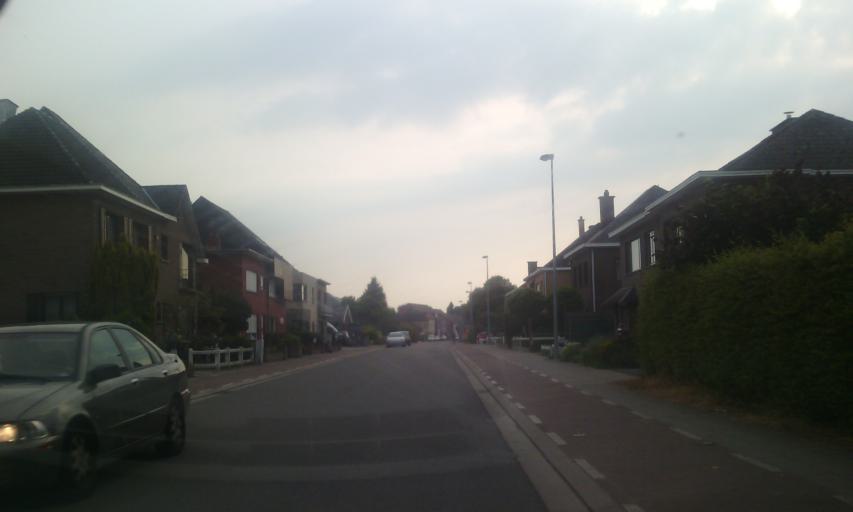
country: BE
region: Flanders
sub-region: Provincie Oost-Vlaanderen
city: Lede
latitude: 50.9635
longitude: 4.0136
